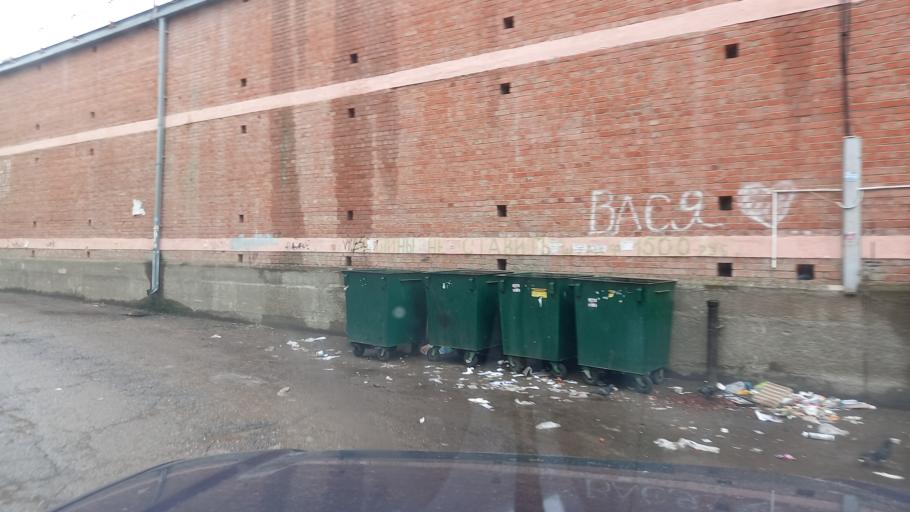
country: RU
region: Krasnodarskiy
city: Pashkovskiy
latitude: 45.0190
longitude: 39.0403
